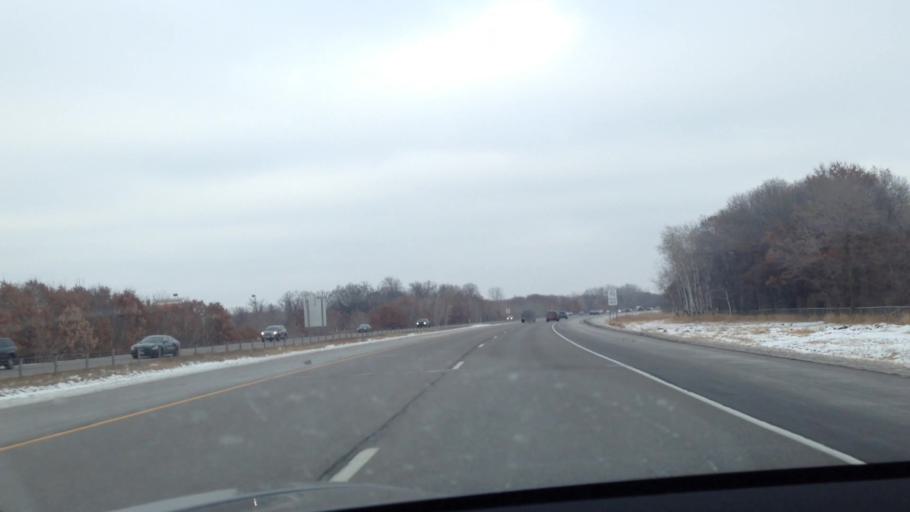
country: US
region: Minnesota
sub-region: Anoka County
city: Circle Pines
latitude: 45.1636
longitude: -93.1570
